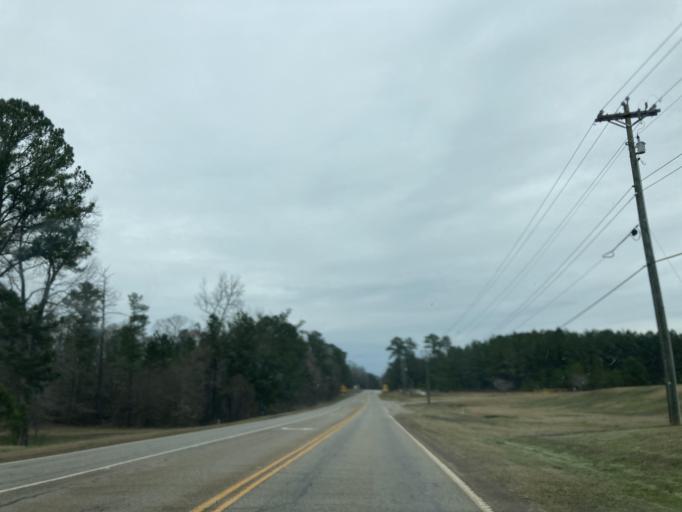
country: US
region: Georgia
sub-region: Jones County
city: Gray
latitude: 32.9869
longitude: -83.6042
